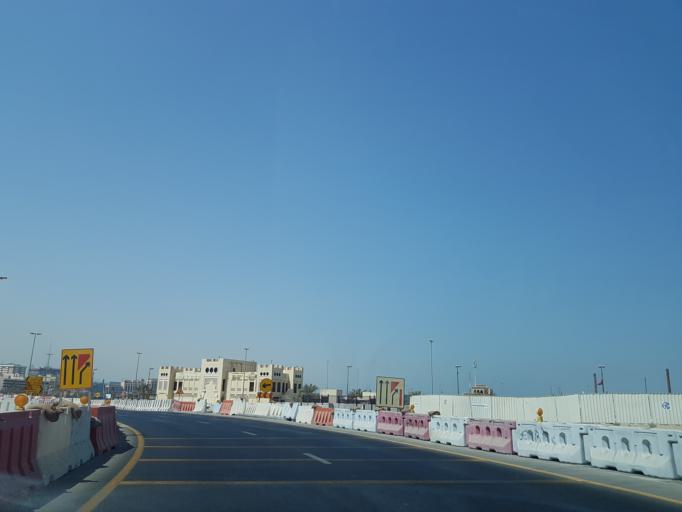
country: AE
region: Ash Shariqah
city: Sharjah
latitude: 25.2758
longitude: 55.2964
